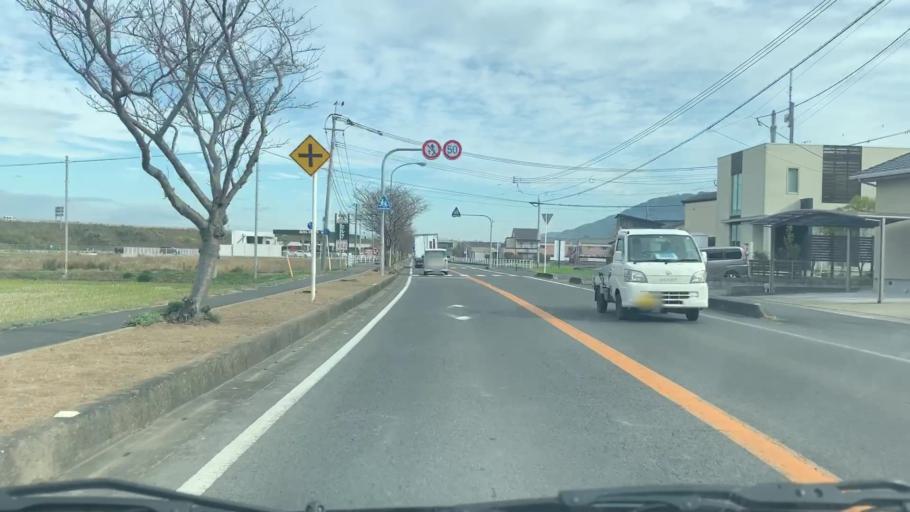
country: JP
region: Saga Prefecture
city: Karatsu
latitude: 33.4106
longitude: 129.9916
